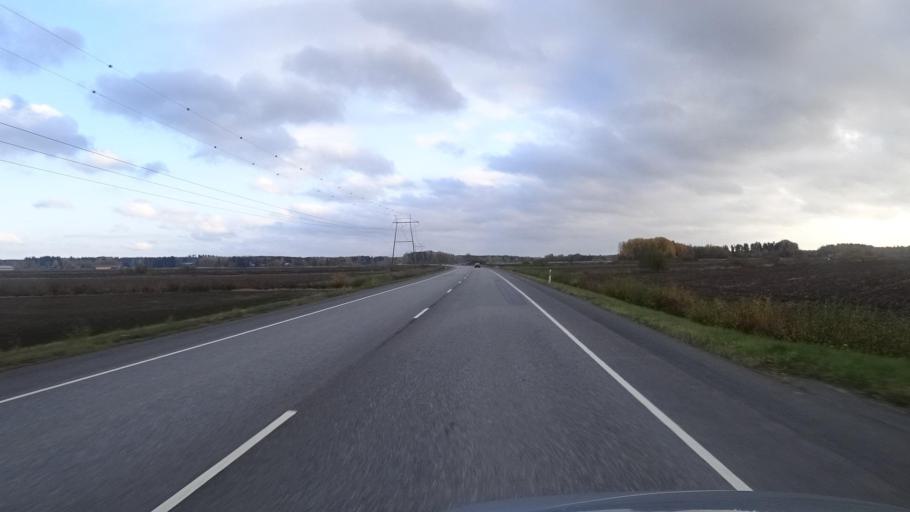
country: FI
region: Satakunta
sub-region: Rauma
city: Saekylae
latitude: 61.0341
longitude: 22.3905
